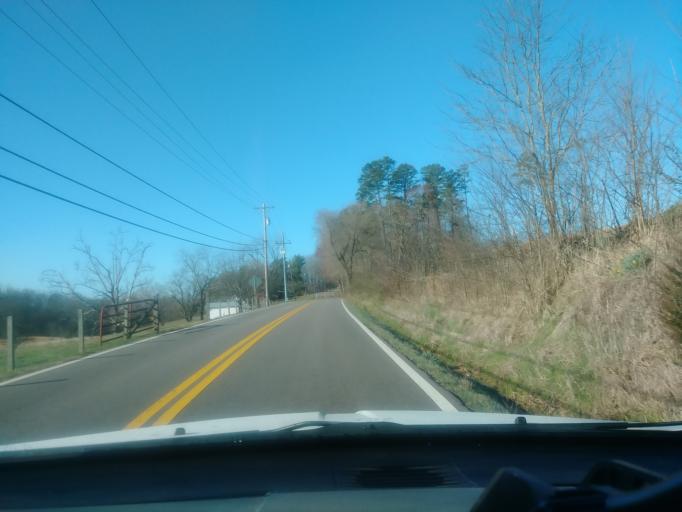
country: US
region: Tennessee
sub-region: Greene County
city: Mosheim
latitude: 36.1187
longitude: -82.9410
